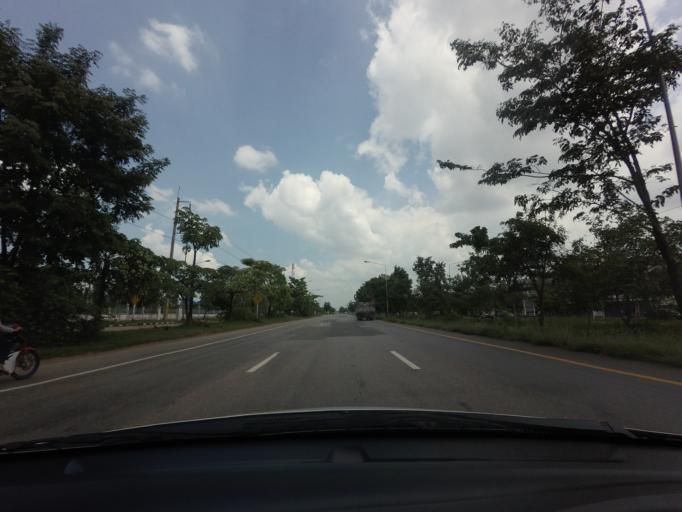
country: TH
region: Prachin Buri
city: Kabin Buri
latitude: 13.9492
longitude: 101.7145
